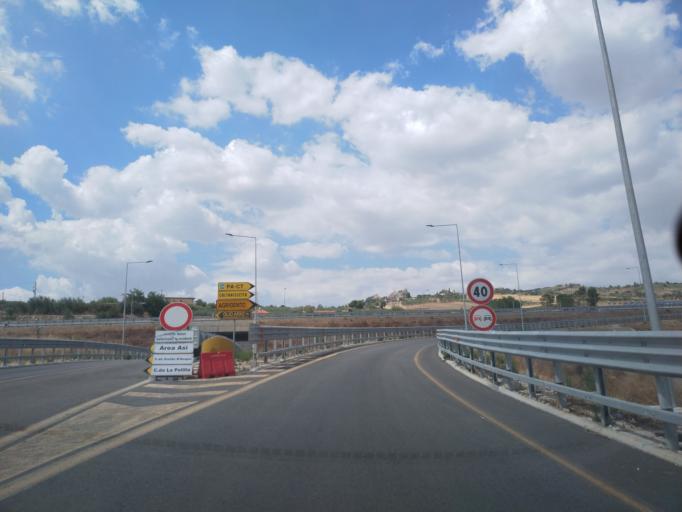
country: IT
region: Sicily
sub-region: Provincia di Caltanissetta
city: San Cataldo
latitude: 37.4494
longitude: 13.9703
